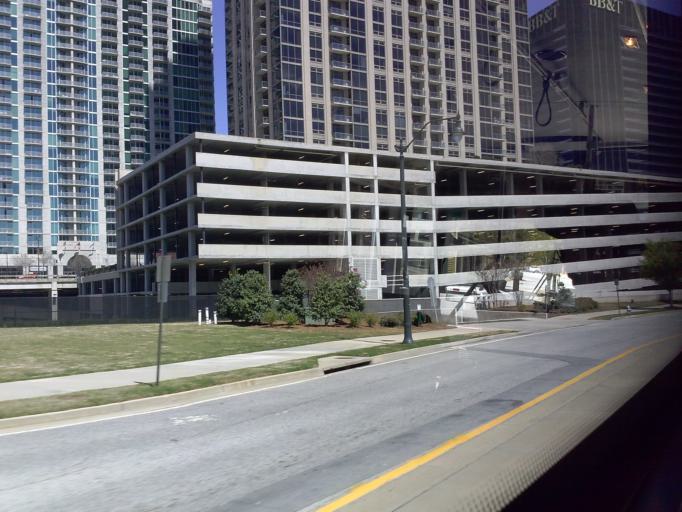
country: US
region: Georgia
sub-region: Fulton County
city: Atlanta
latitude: 33.7898
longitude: -84.3984
